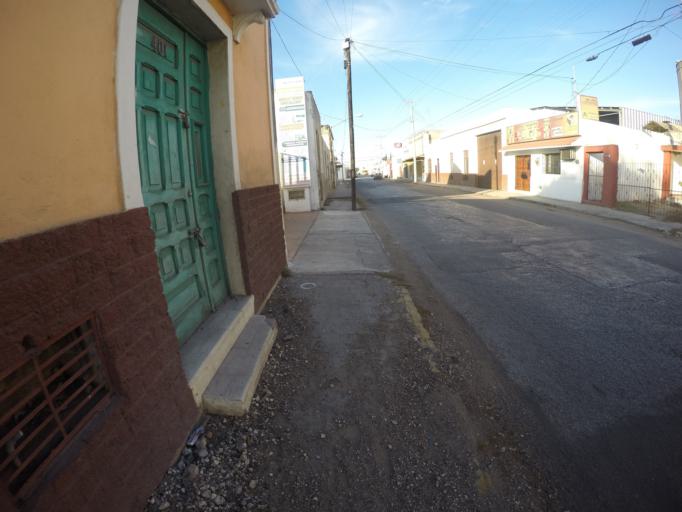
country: MX
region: Yucatan
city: Merida
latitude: 20.9790
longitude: -89.6153
